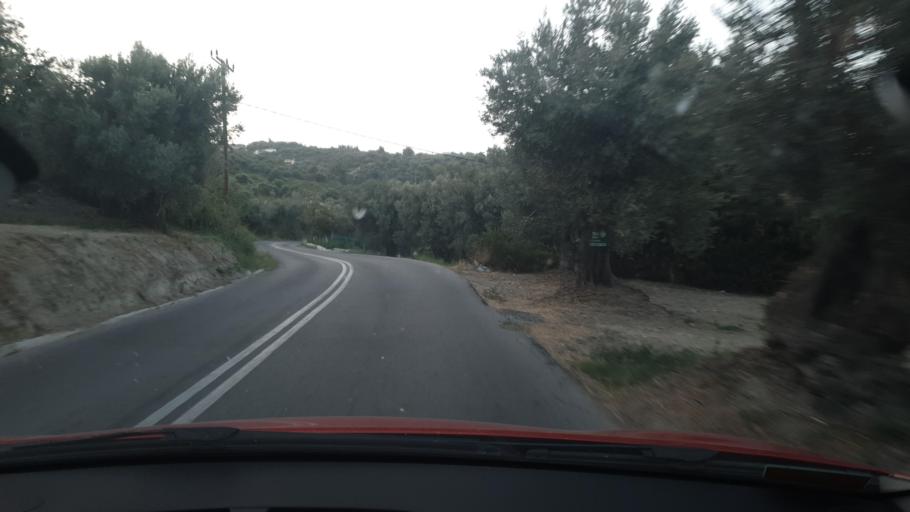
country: GR
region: Central Greece
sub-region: Nomos Evvoias
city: Kymi
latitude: 38.6307
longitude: 24.1175
